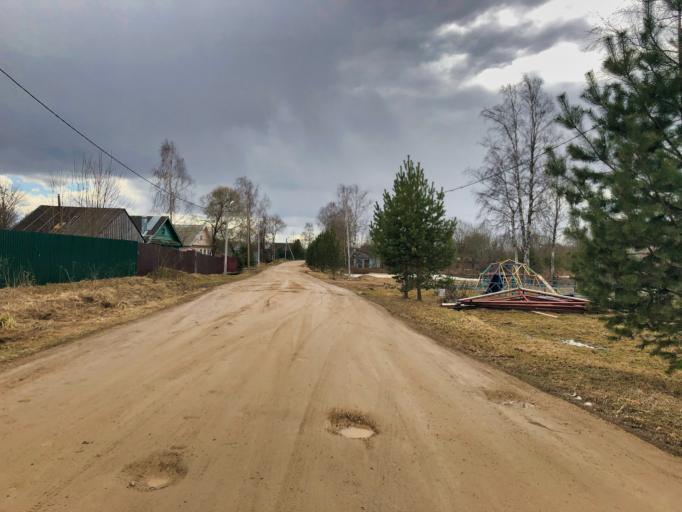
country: RU
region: Tverskaya
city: Rzhev
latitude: 56.2285
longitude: 34.3097
